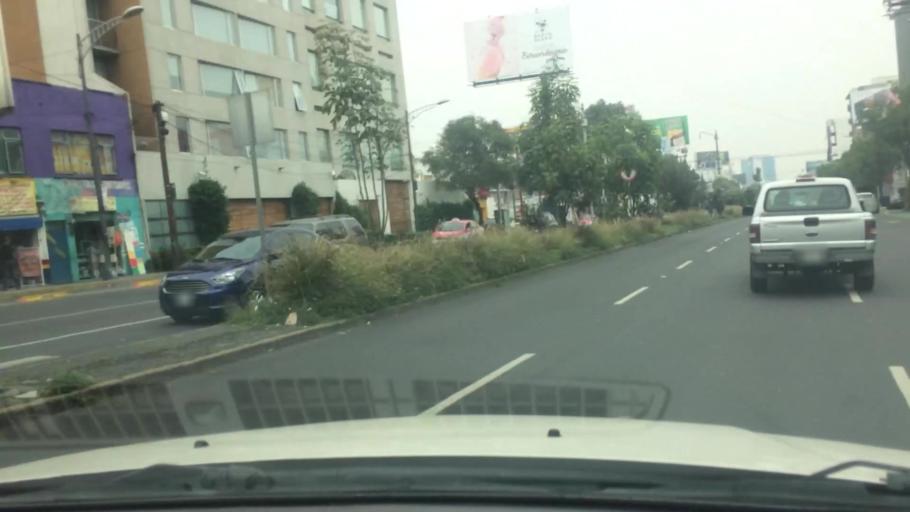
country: MX
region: Mexico City
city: Alvaro Obregon
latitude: 19.3708
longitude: -99.1949
